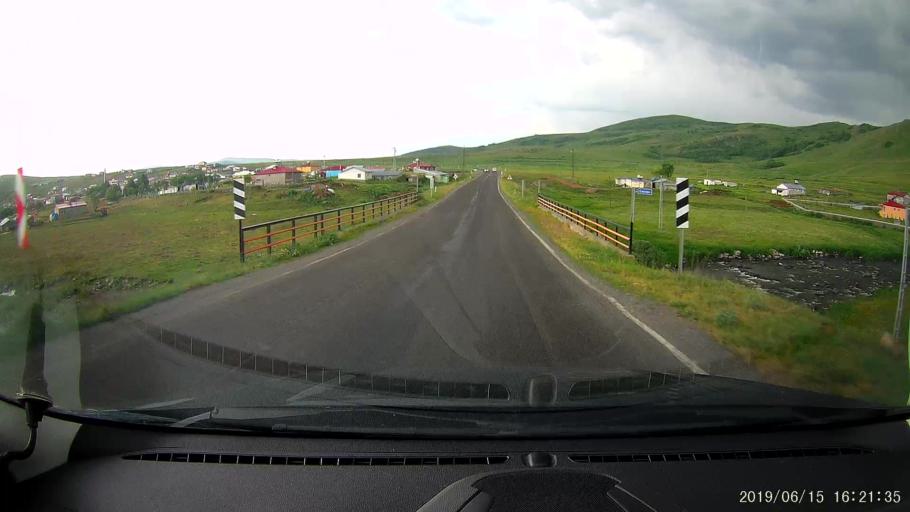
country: TR
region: Ardahan
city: Hanak
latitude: 41.1983
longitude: 42.8464
